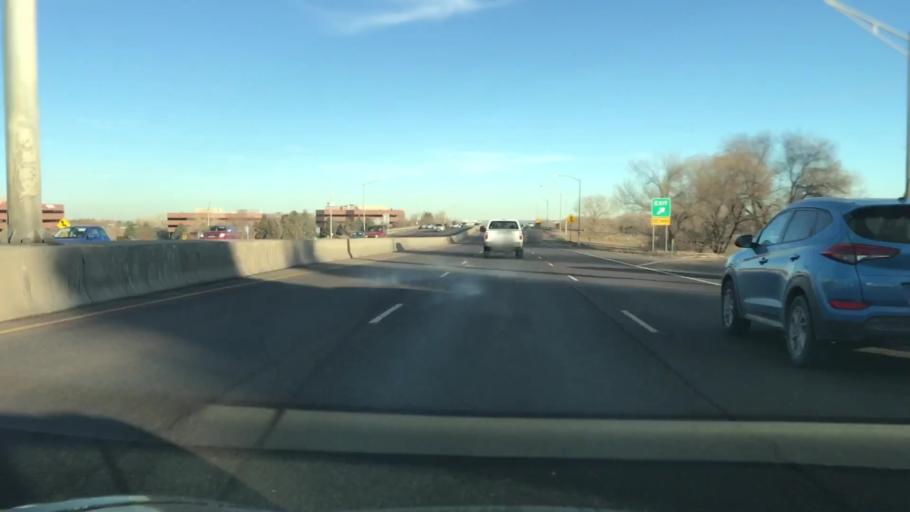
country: US
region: Colorado
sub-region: Jefferson County
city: Lakewood
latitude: 39.7250
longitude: -105.1128
